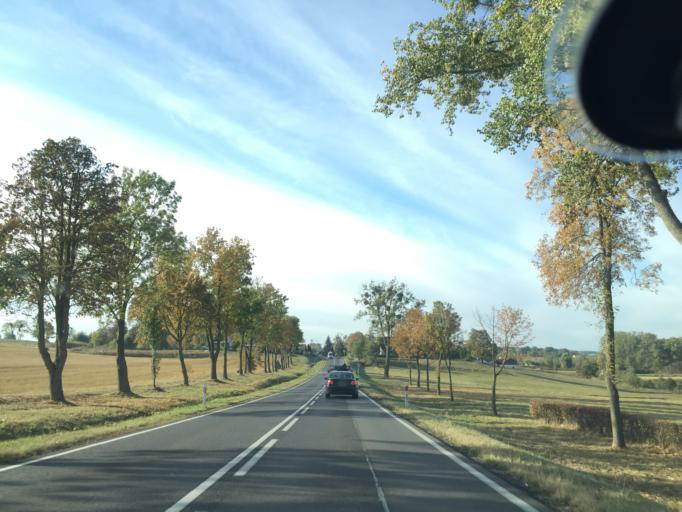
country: PL
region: Warmian-Masurian Voivodeship
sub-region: Powiat lidzbarski
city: Lidzbark Warminski
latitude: 54.0869
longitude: 20.5423
